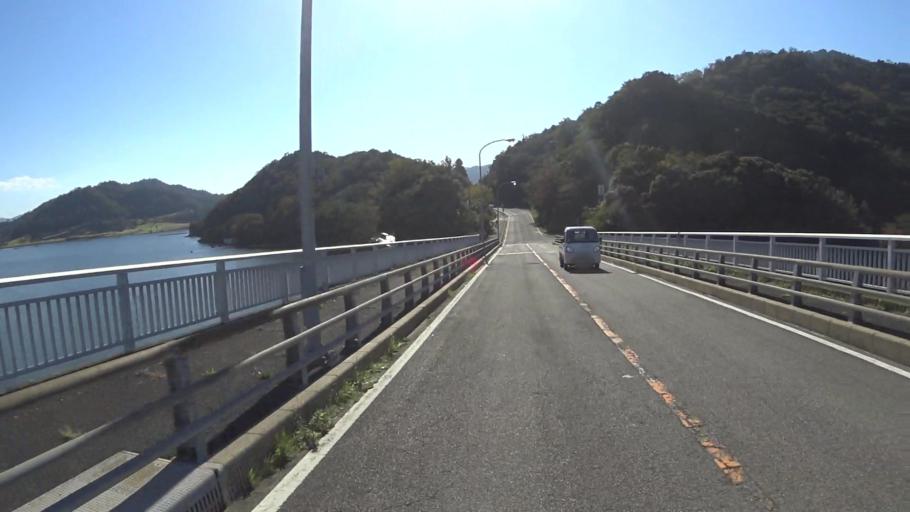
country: JP
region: Hyogo
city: Toyooka
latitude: 35.6424
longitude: 134.8998
